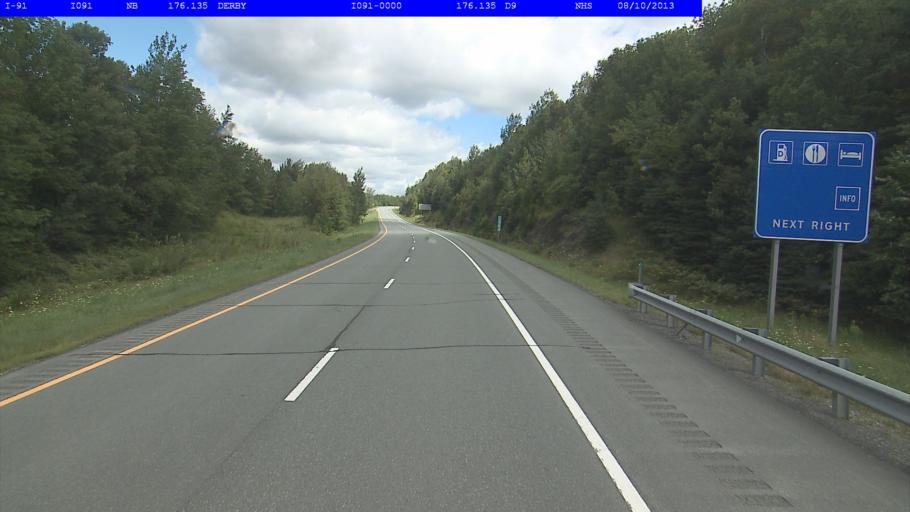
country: US
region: Vermont
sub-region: Orleans County
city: Newport
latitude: 44.9916
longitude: -72.1023
